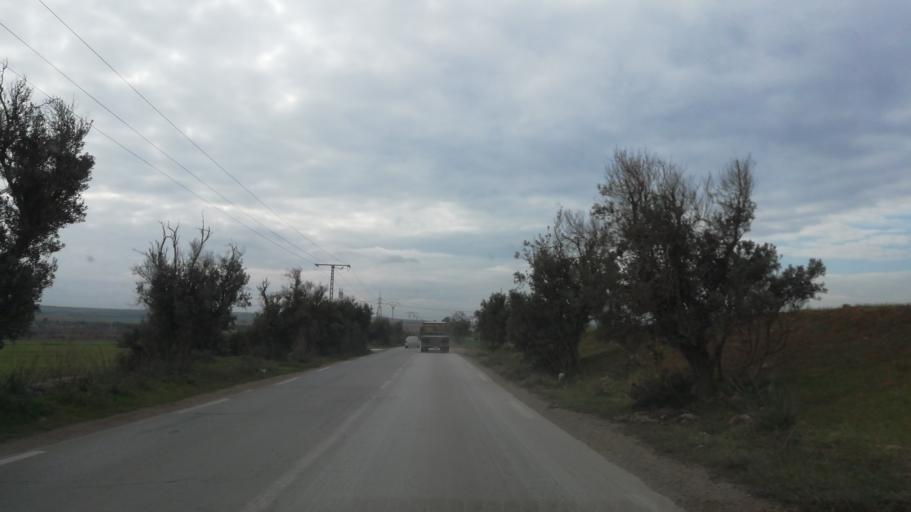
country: DZ
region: Oran
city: Ain el Bya
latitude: 35.7786
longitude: -0.3453
